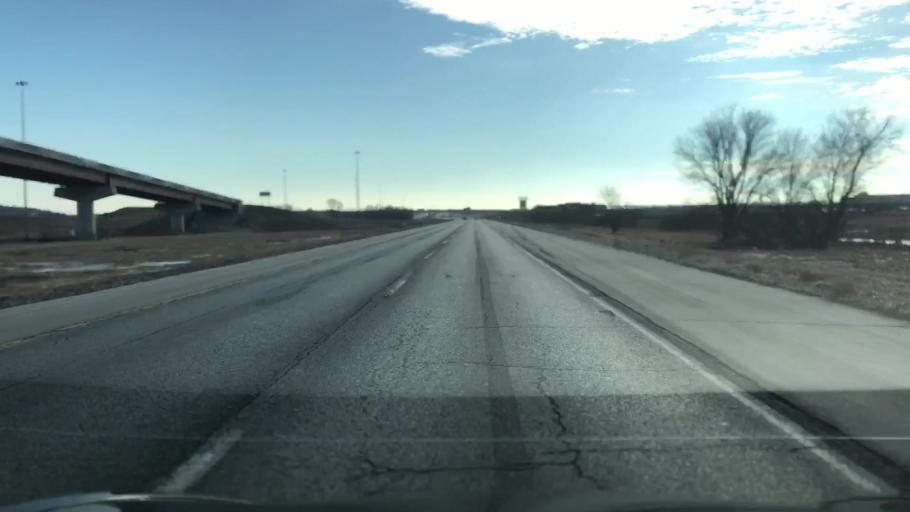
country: US
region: Iowa
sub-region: Pottawattamie County
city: Council Bluffs
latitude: 41.2290
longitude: -95.8414
